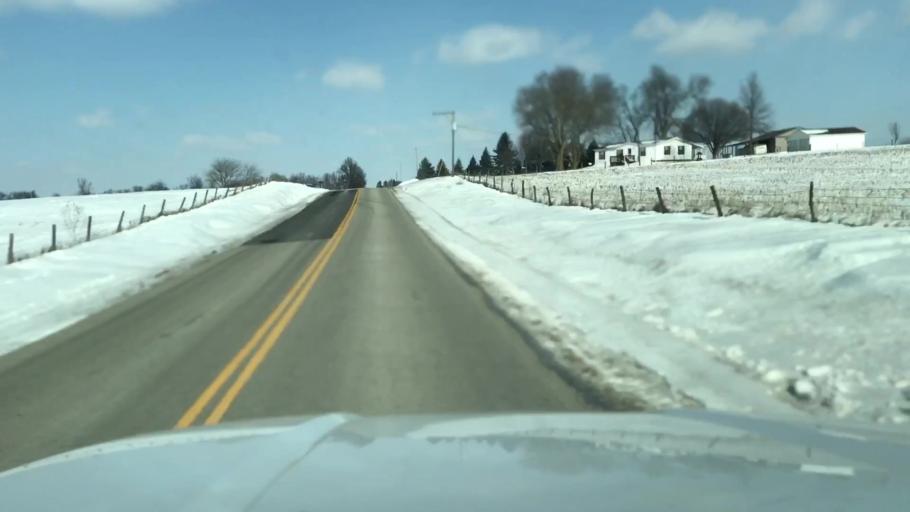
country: US
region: Missouri
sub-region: Nodaway County
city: Maryville
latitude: 40.3642
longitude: -94.7218
